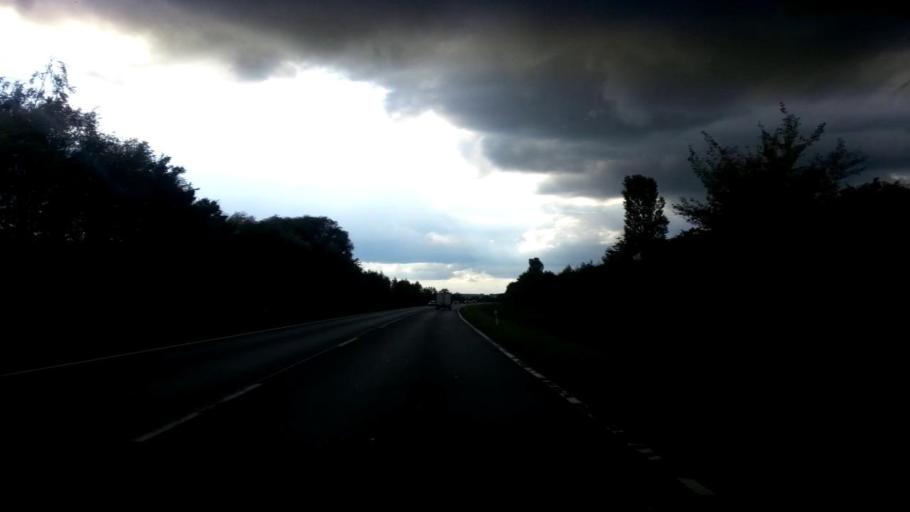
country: DE
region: Bavaria
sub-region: Regierungsbezirk Mittelfranken
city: Adelsdorf
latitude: 49.7005
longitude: 10.8727
